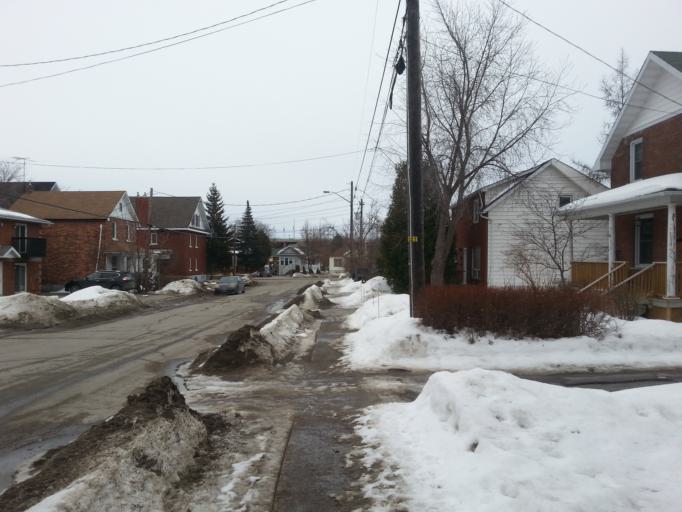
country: CA
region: Ontario
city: Greater Sudbury
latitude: 46.4850
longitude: -80.9932
